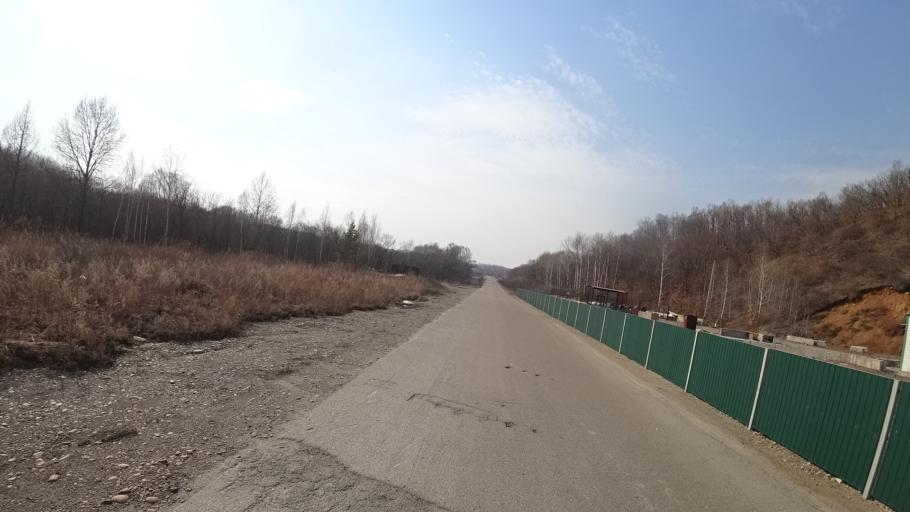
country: RU
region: Amur
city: Novobureyskiy
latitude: 49.7949
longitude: 129.9606
